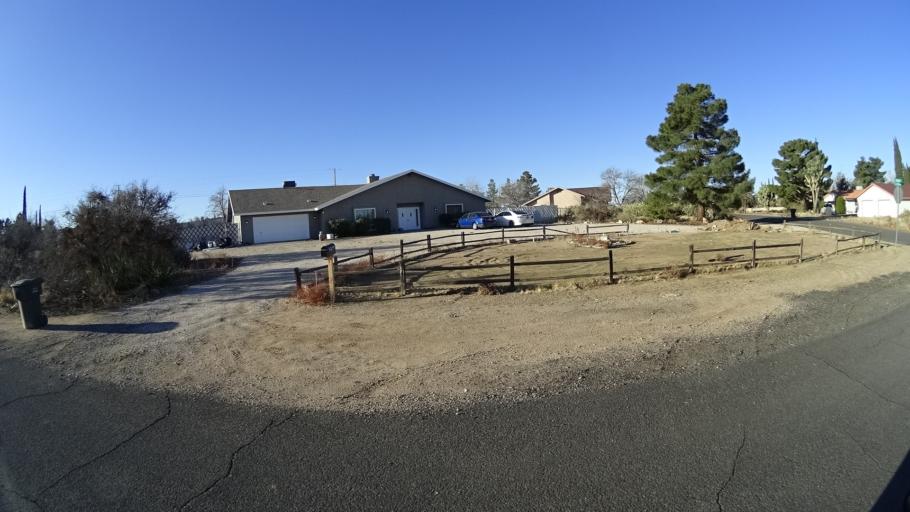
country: US
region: Arizona
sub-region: Mohave County
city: Kingman
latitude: 35.2046
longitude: -114.0058
